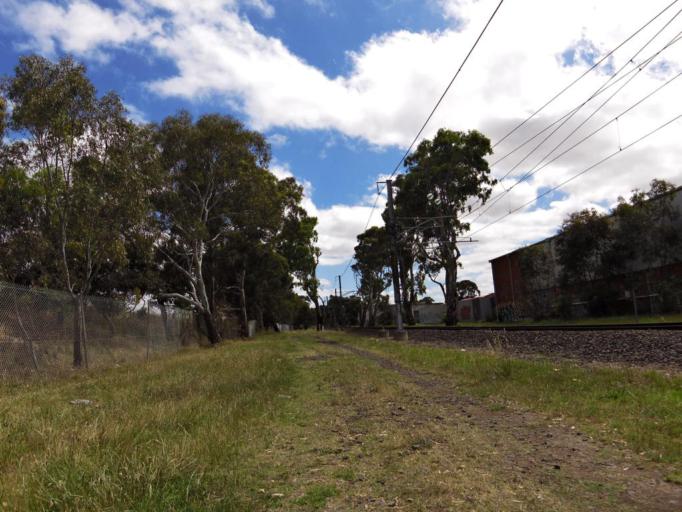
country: AU
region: Victoria
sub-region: Hume
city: Campbellfield
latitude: -37.6986
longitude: 144.9585
